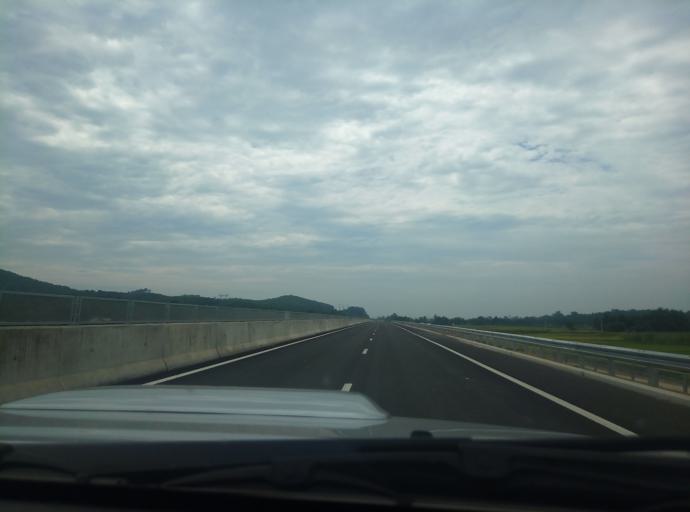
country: VN
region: Quang Nam
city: Tam Ky
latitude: 15.5065
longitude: 108.5197
